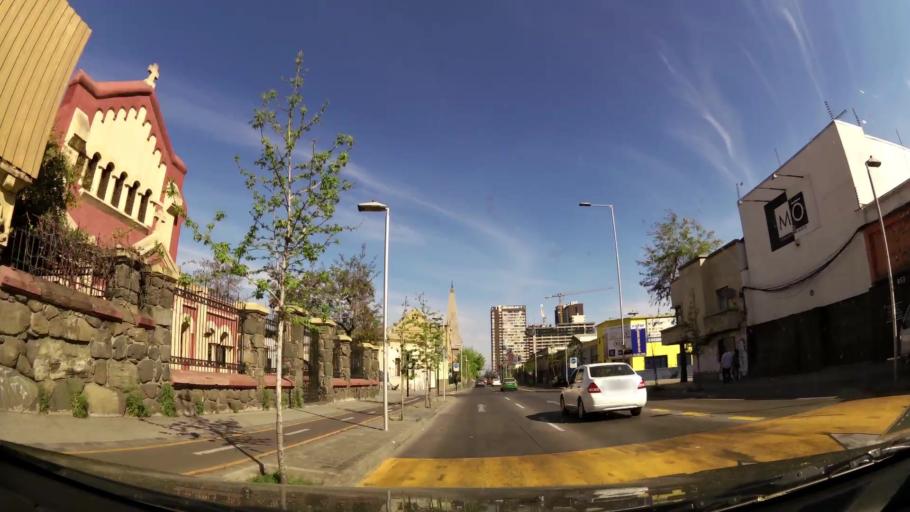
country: CL
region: Santiago Metropolitan
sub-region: Provincia de Santiago
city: Santiago
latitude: -33.4549
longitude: -70.6402
